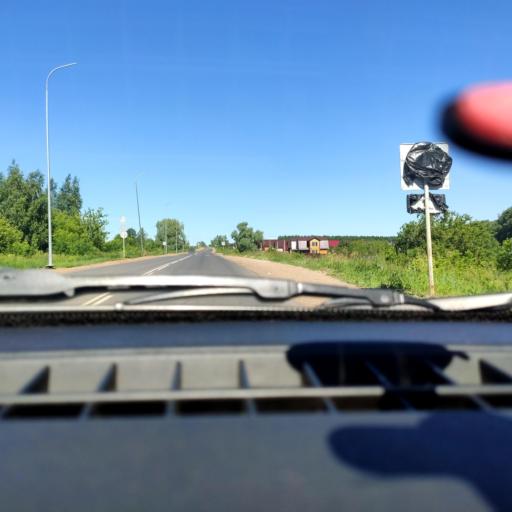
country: RU
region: Bashkortostan
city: Iglino
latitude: 54.8398
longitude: 56.3918
